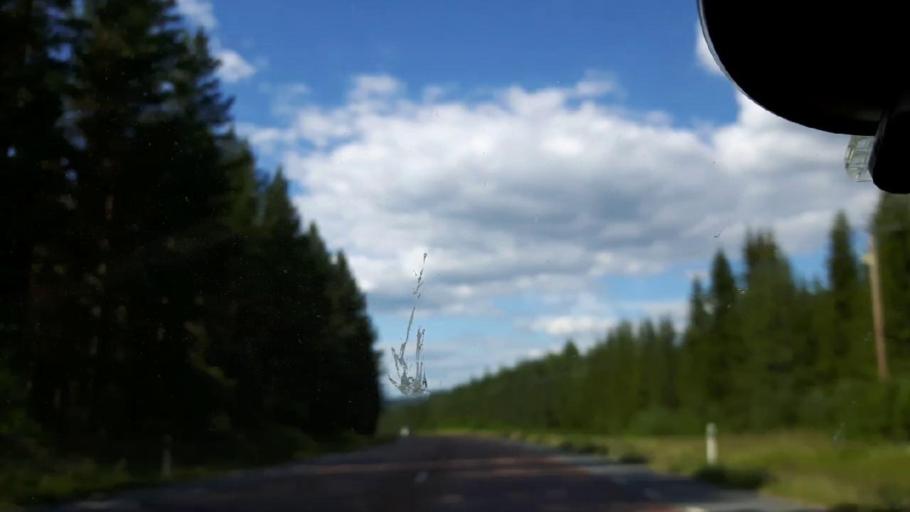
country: SE
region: Jaemtland
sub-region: Braecke Kommun
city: Braecke
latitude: 62.8070
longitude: 15.3682
